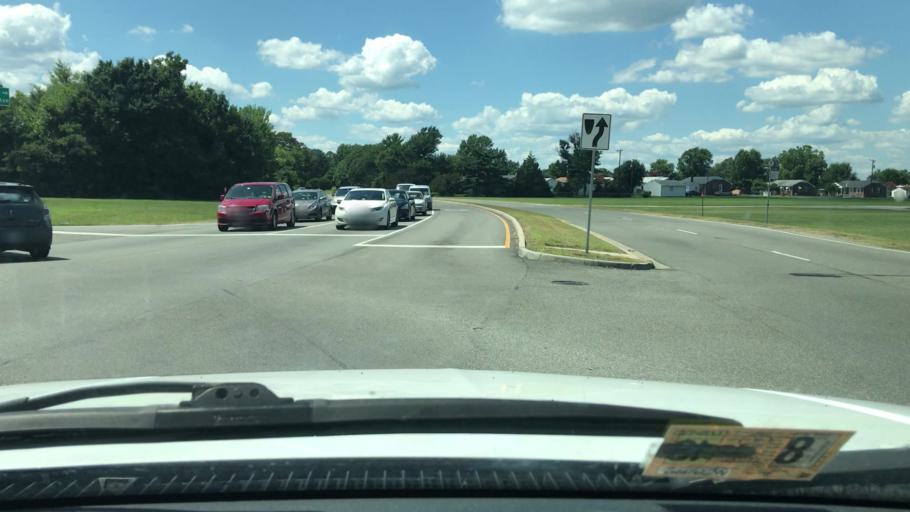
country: US
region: Virginia
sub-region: Henrico County
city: East Highland Park
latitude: 37.5718
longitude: -77.3824
